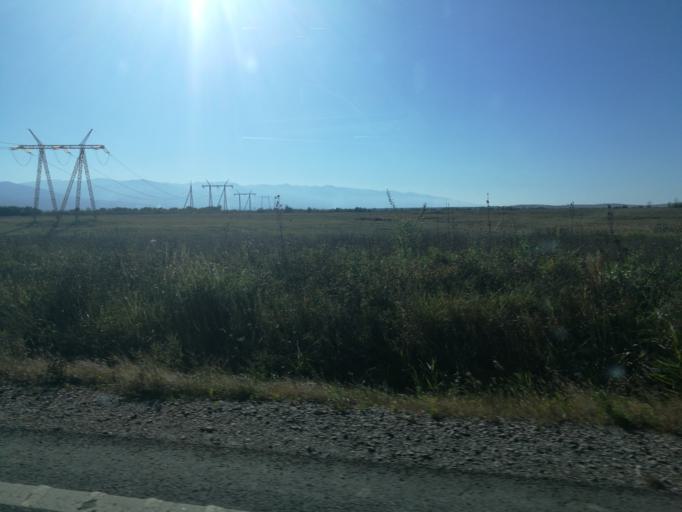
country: RO
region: Brasov
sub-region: Comuna Sinca Veche
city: Sinca Veche
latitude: 45.7978
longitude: 25.1800
